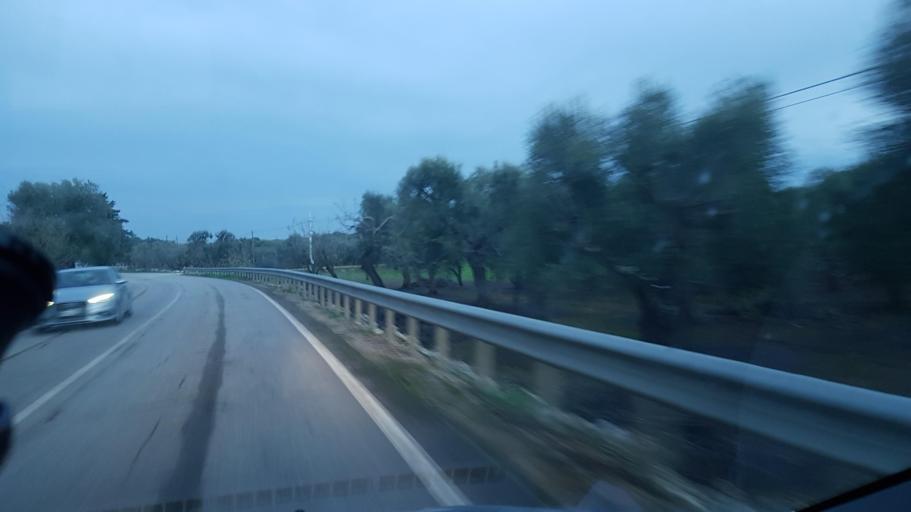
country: IT
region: Apulia
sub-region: Provincia di Brindisi
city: San Michele Salentino
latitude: 40.6411
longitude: 17.5795
